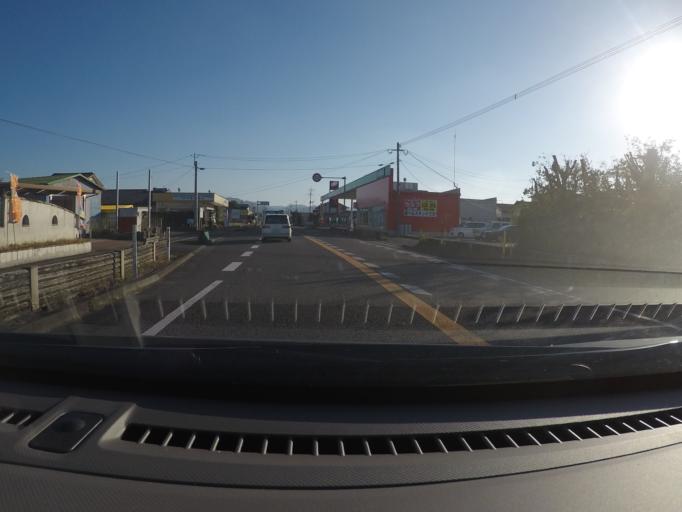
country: JP
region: Kagoshima
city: Izumi
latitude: 32.1202
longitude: 130.3400
